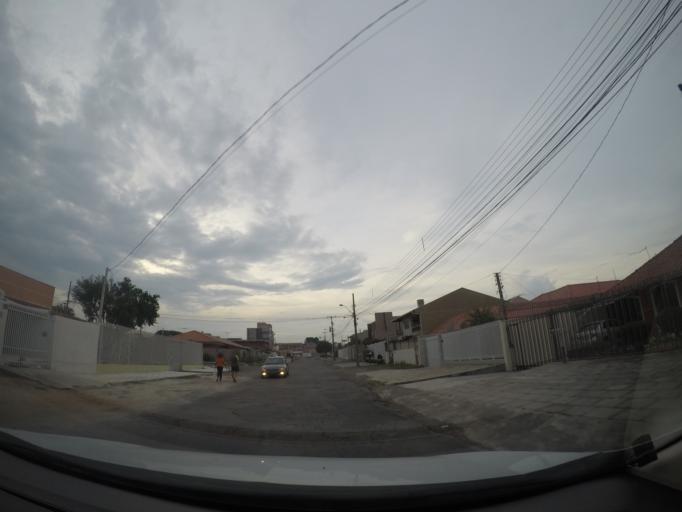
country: BR
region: Parana
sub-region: Sao Jose Dos Pinhais
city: Sao Jose dos Pinhais
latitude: -25.5224
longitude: -49.2328
